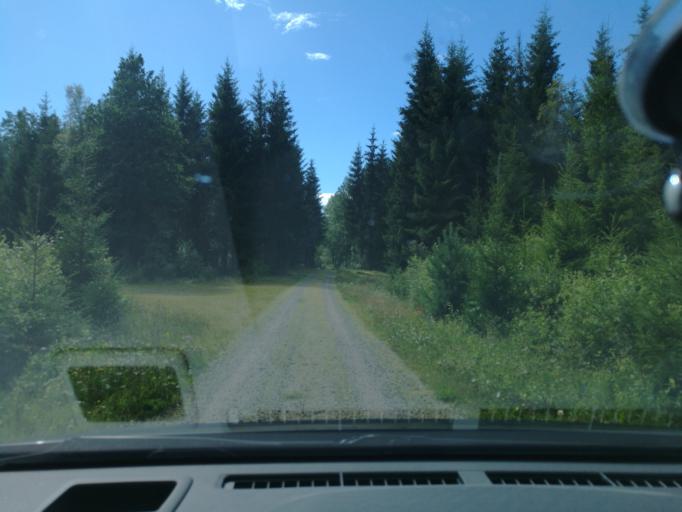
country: SE
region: Kronoberg
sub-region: Alvesta Kommun
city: Vislanda
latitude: 56.6972
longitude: 14.4058
